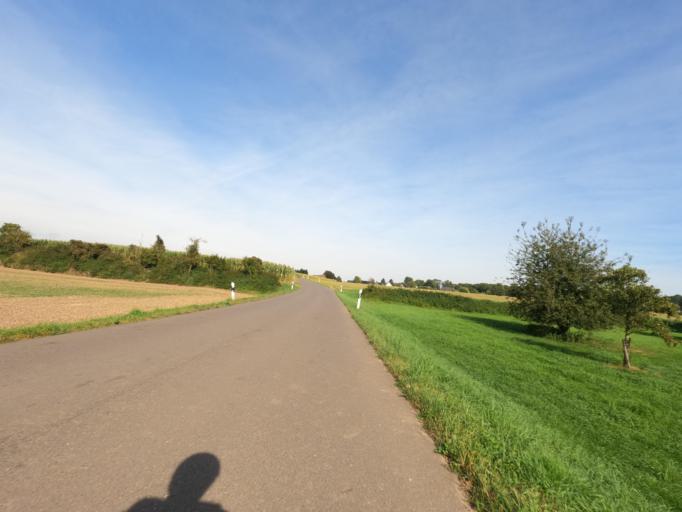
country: DE
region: North Rhine-Westphalia
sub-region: Regierungsbezirk Koln
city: Linnich
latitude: 50.9899
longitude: 6.2866
